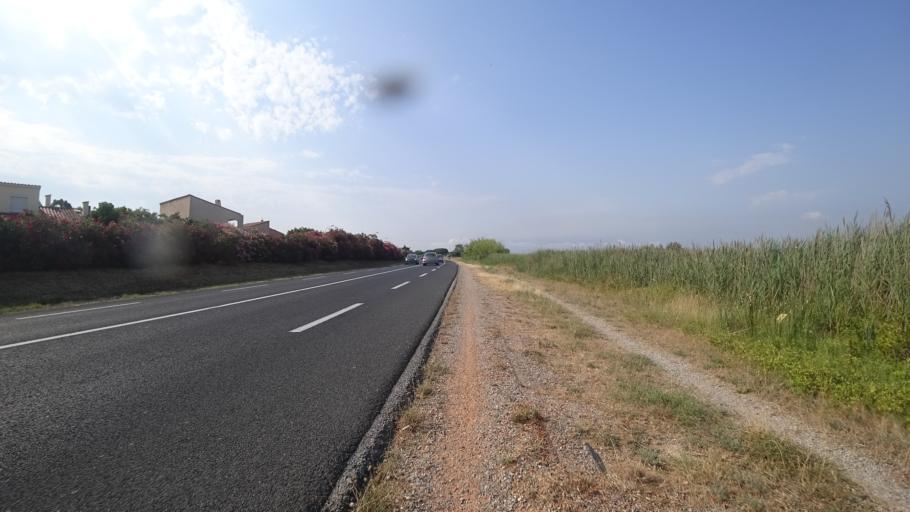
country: FR
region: Languedoc-Roussillon
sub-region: Departement des Pyrenees-Orientales
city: Canet-en-Roussillon
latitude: 42.6815
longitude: 3.0282
